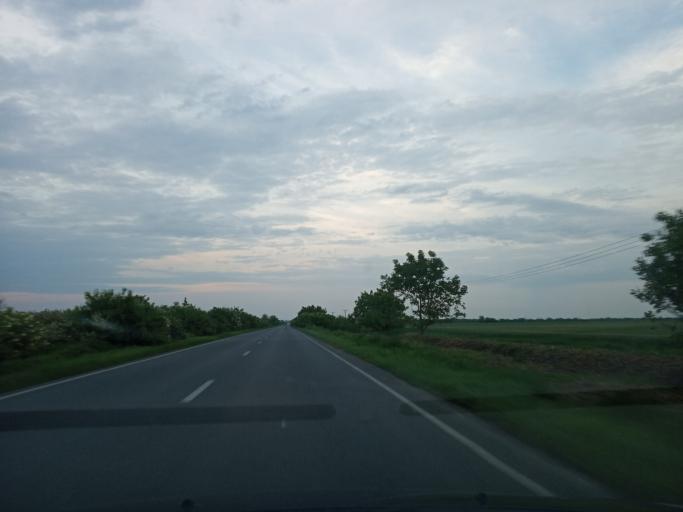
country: RO
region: Timis
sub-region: Comuna Voiteg
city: Voiteg
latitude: 45.4493
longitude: 21.2334
